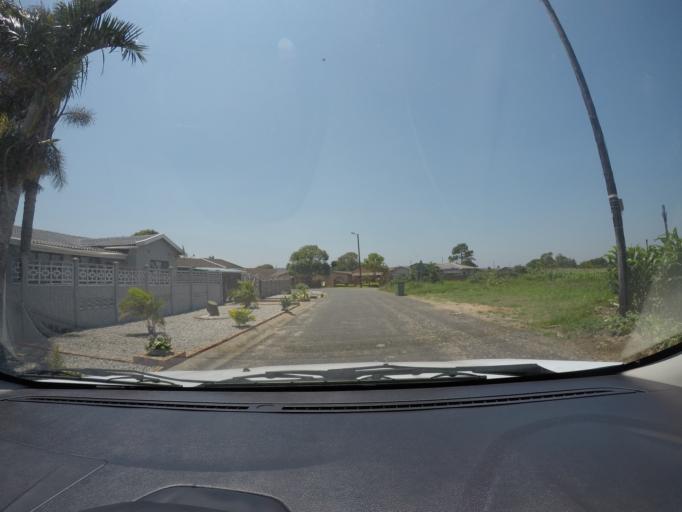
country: ZA
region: KwaZulu-Natal
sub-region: uThungulu District Municipality
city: eSikhawini
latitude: -28.8915
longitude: 31.8839
